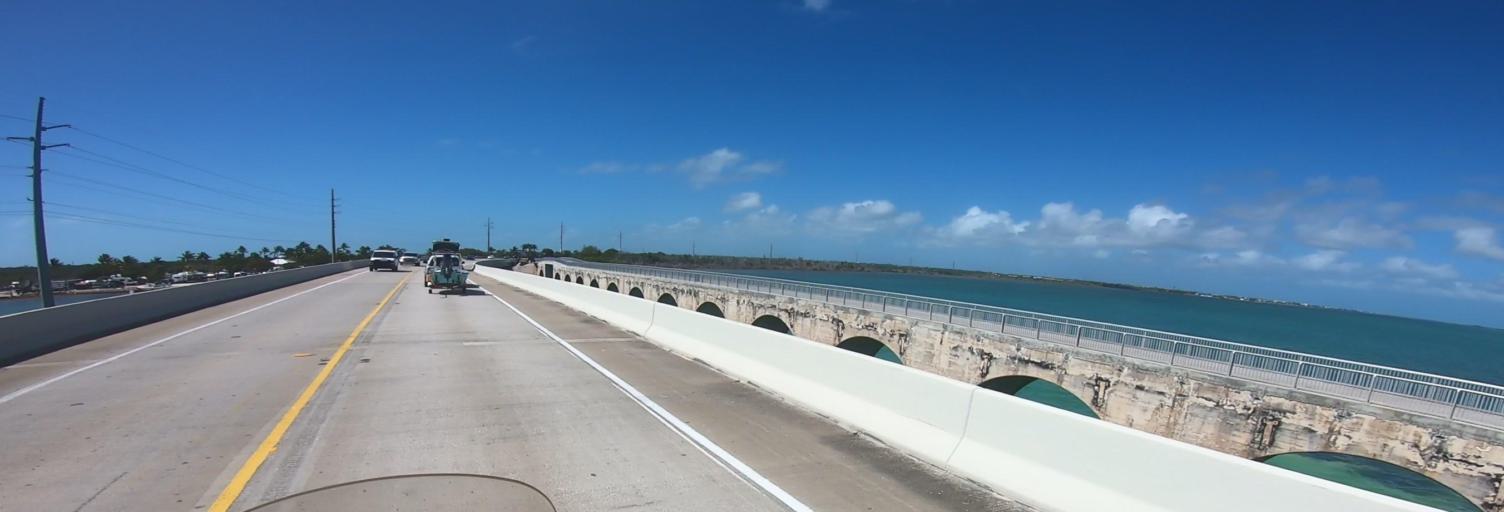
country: US
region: Florida
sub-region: Monroe County
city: Big Pine Key
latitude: 24.6485
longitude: -81.3274
